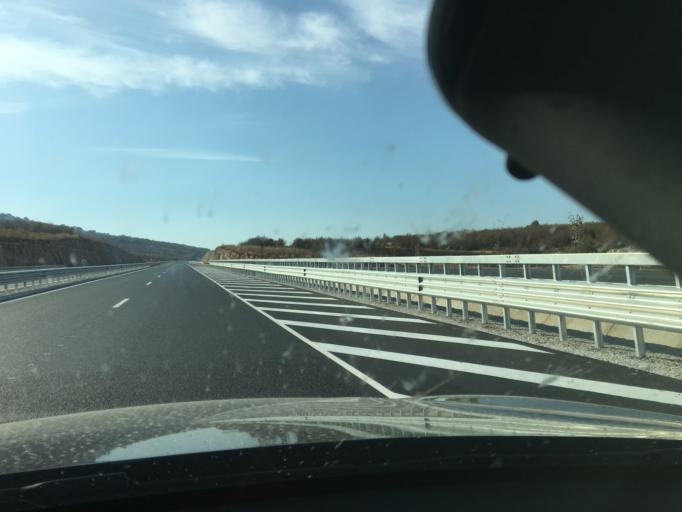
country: BG
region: Lovech
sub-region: Obshtina Yablanitsa
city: Yablanitsa
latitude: 43.0533
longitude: 24.1960
